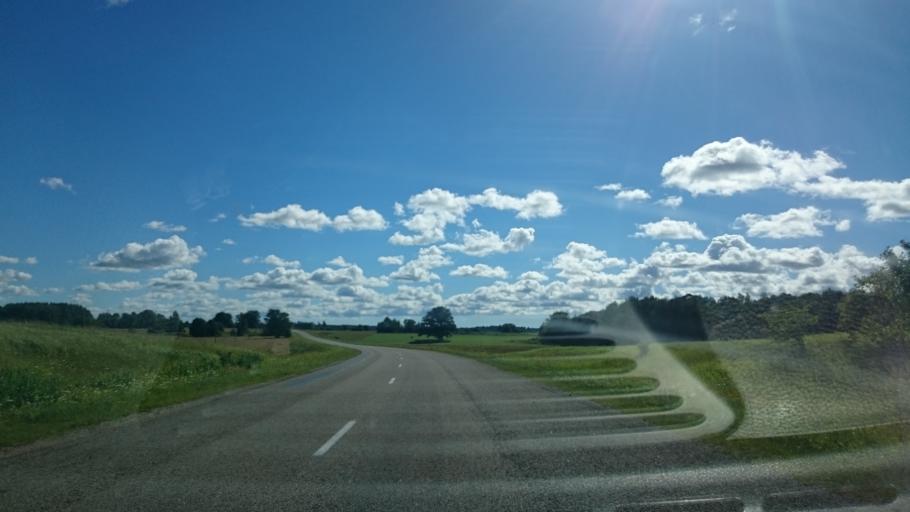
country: LV
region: Aizpute
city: Aizpute
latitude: 56.7710
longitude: 21.6261
